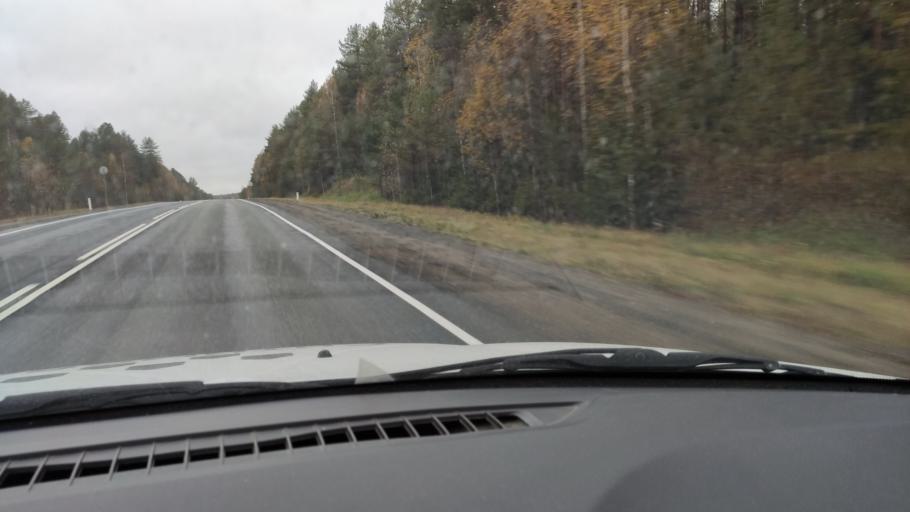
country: RU
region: Kirov
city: Dubrovka
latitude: 58.9060
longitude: 51.2208
